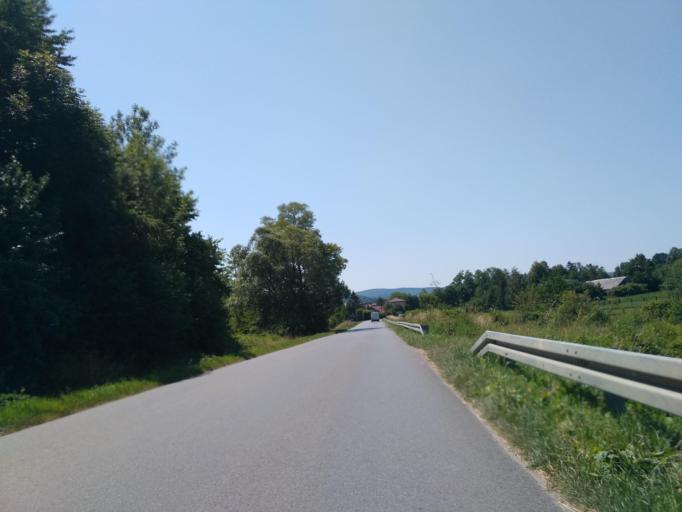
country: PL
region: Subcarpathian Voivodeship
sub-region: Powiat sanocki
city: Niebieszczany
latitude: 49.5364
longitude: 22.1292
